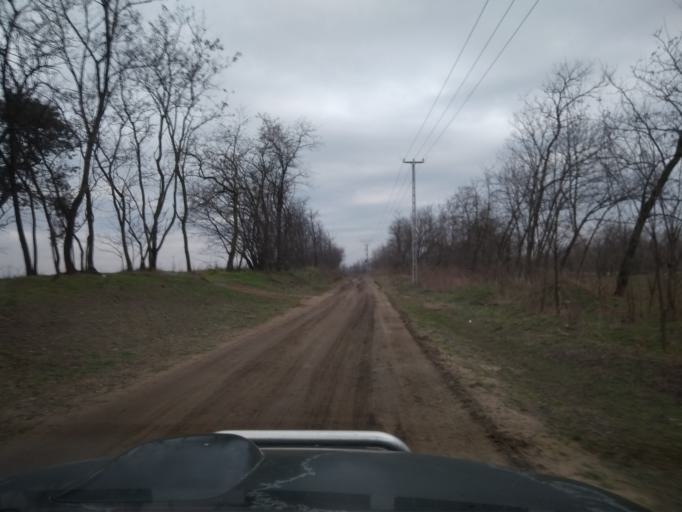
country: HU
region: Szabolcs-Szatmar-Bereg
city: Nyirpazony
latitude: 47.9980
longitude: 21.7886
